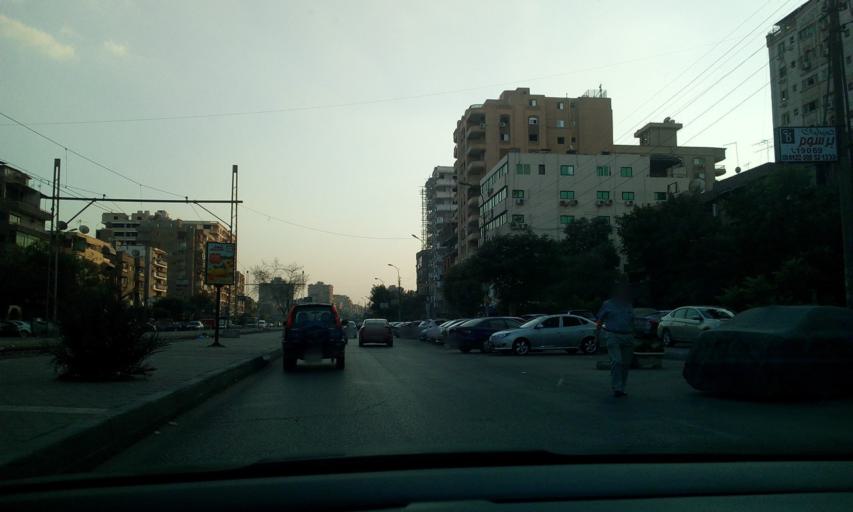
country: EG
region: Muhafazat al Qalyubiyah
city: Al Khankah
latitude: 30.1149
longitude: 31.3509
